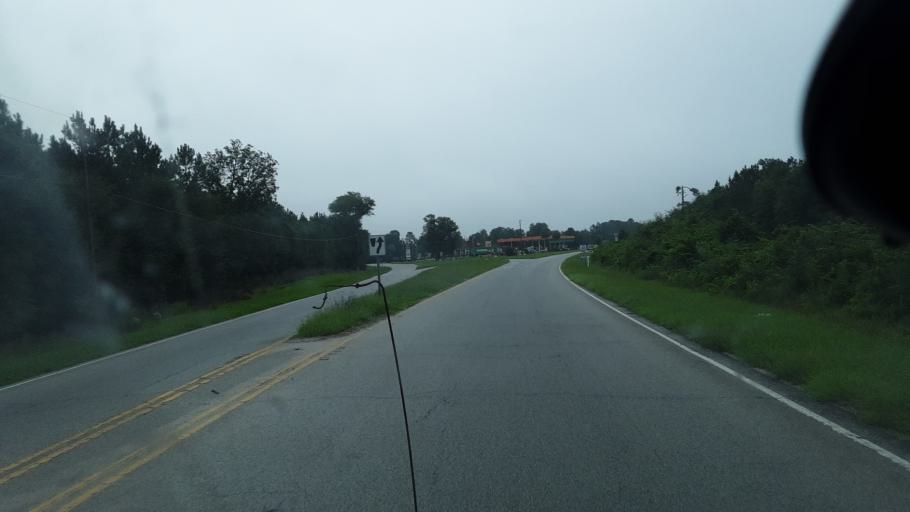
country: US
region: South Carolina
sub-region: Florence County
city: Johnsonville
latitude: 33.9133
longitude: -79.4096
